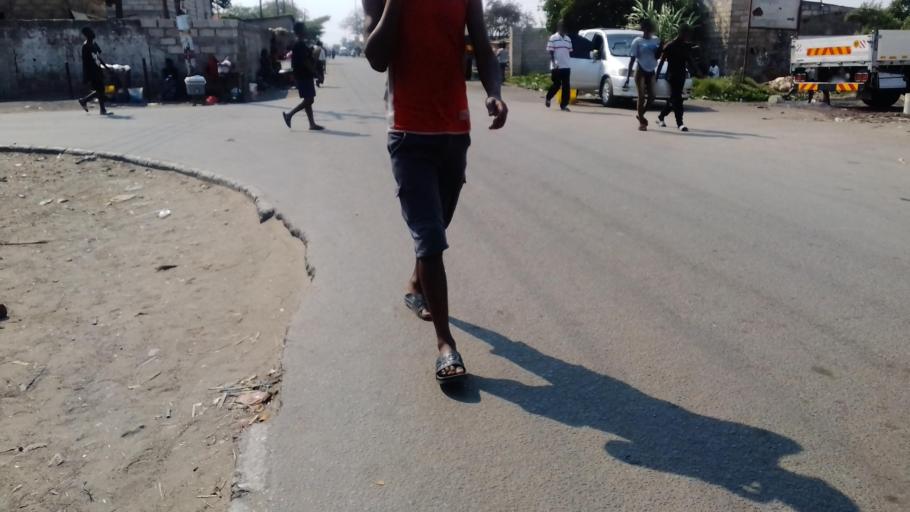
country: ZM
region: Lusaka
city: Lusaka
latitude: -15.4347
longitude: 28.2577
